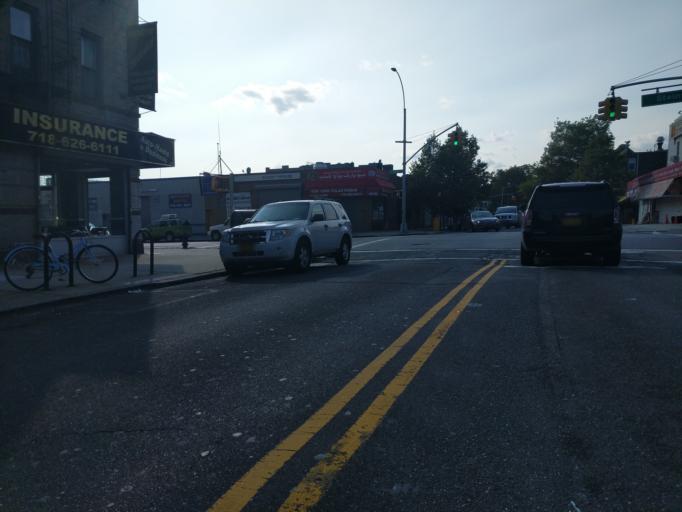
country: US
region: New York
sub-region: Queens County
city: Long Island City
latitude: 40.7535
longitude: -73.9231
